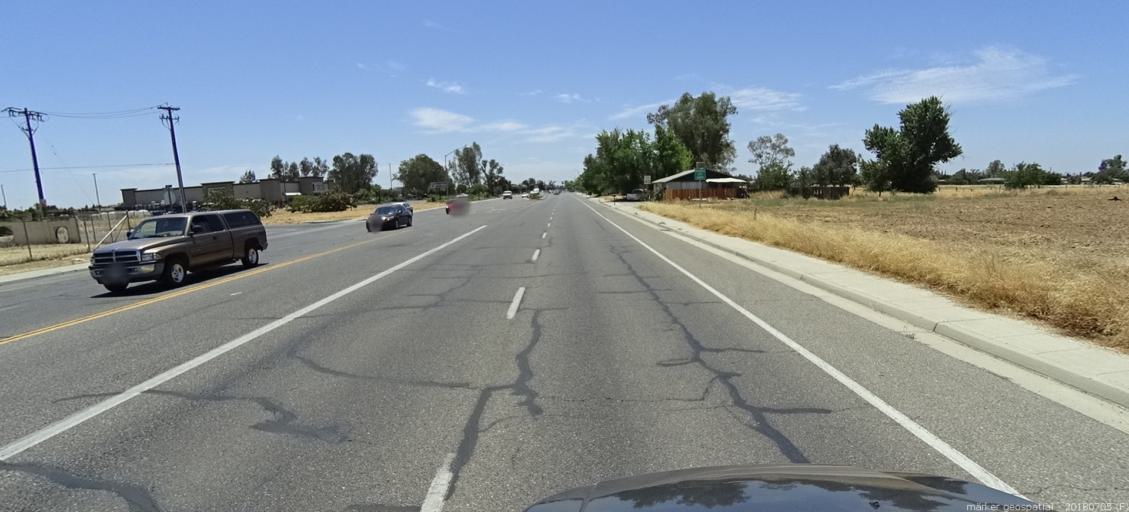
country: US
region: California
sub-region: Madera County
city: Madera
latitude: 36.9833
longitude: -120.0743
